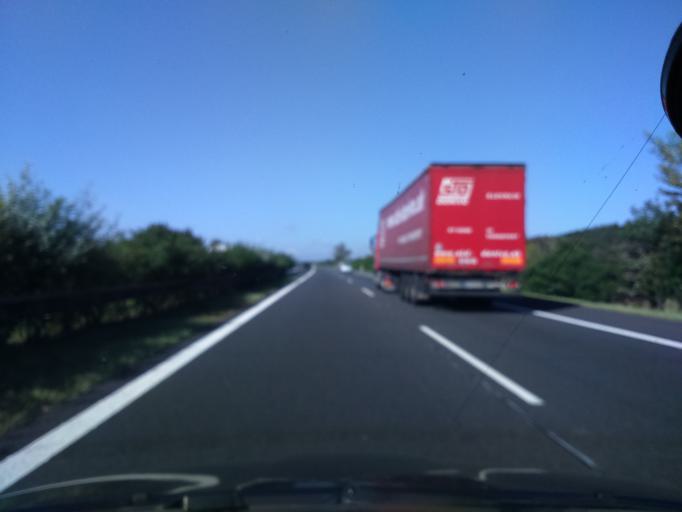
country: CZ
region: Central Bohemia
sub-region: Okres Nymburk
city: Sadska
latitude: 50.1229
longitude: 15.0102
